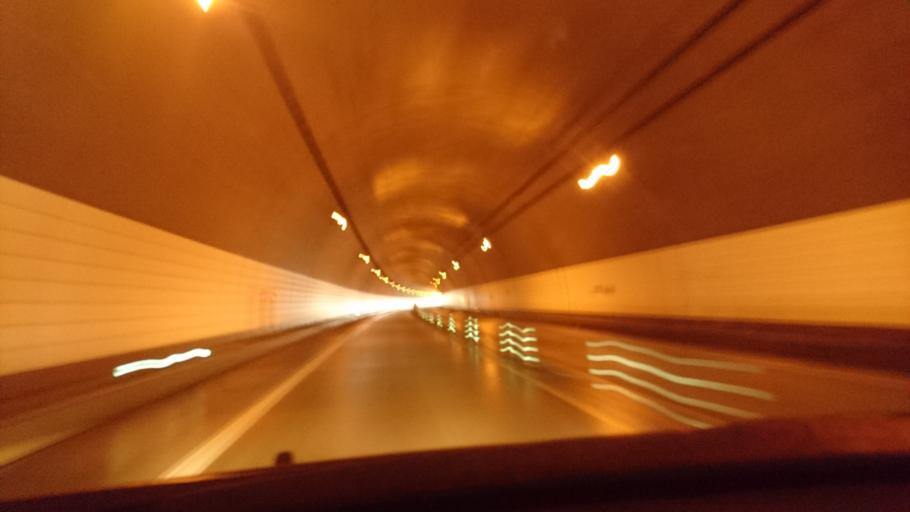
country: JP
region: Iwate
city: Yamada
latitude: 39.4673
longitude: 141.9383
